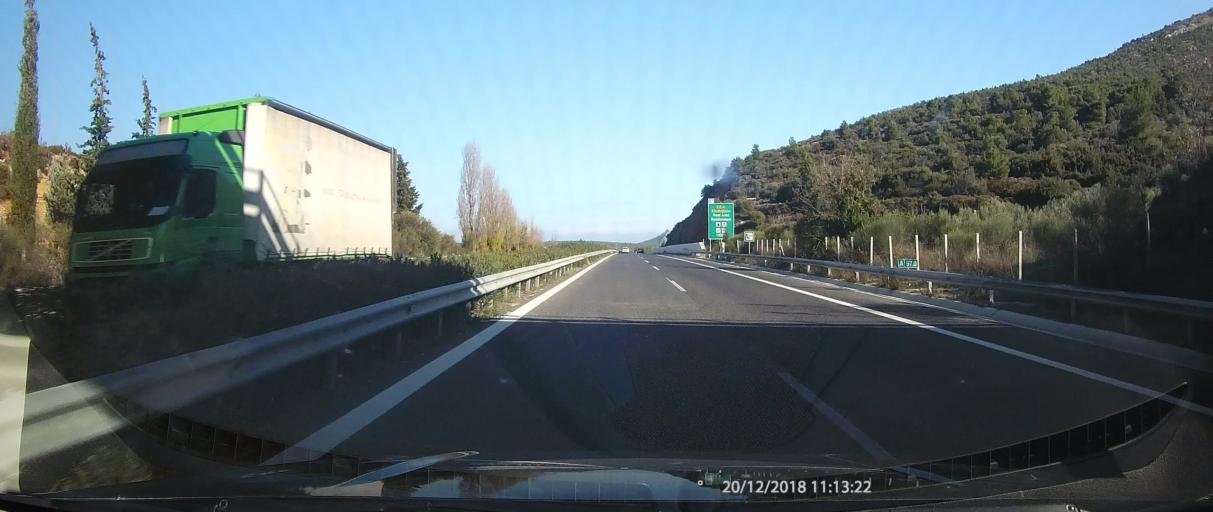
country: GR
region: Peloponnese
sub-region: Nomos Korinthias
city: Khiliomodhi
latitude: 37.8515
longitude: 22.8297
